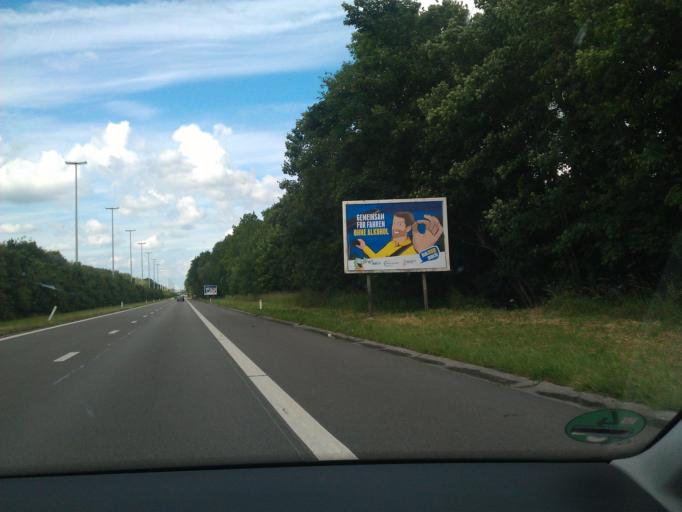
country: BE
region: Wallonia
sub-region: Province de Liege
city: Lontzen
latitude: 50.6614
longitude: 6.0203
